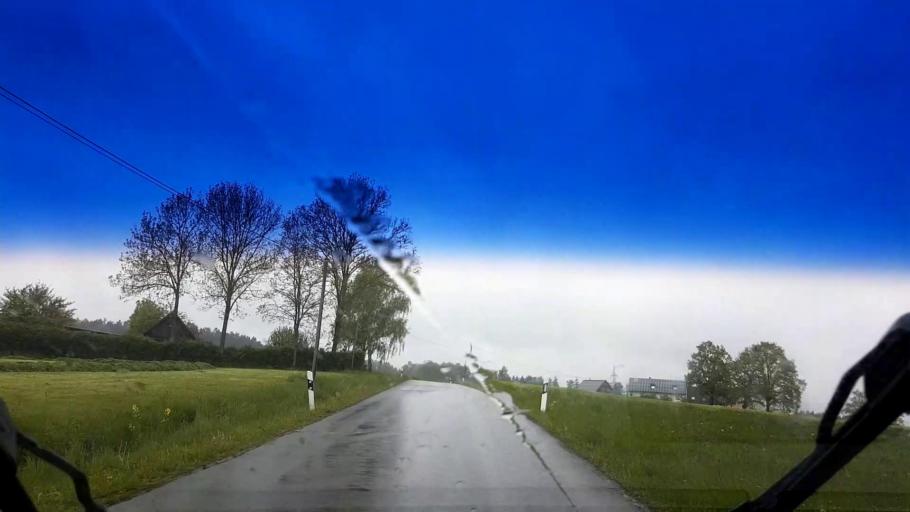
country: DE
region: Bavaria
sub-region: Upper Franconia
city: Bindlach
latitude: 50.0194
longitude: 11.6268
